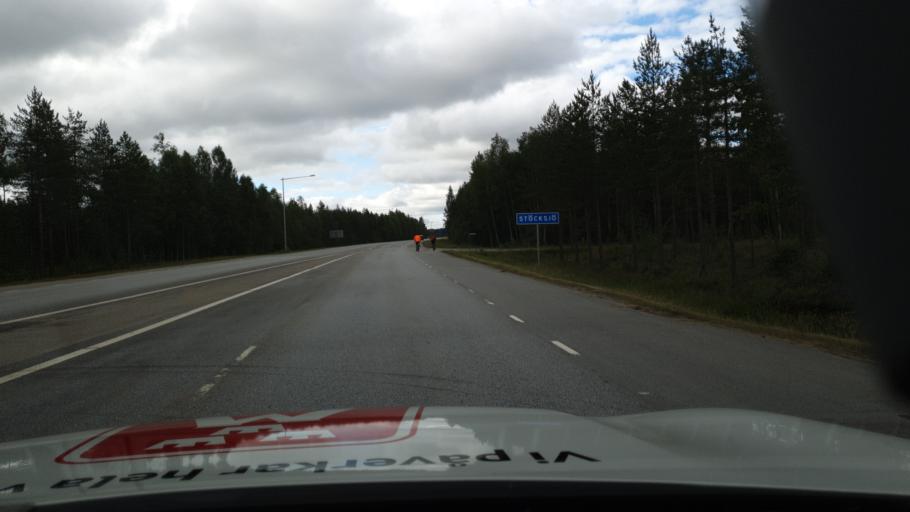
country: SE
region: Vaesterbotten
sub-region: Umea Kommun
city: Roback
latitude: 63.7835
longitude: 20.2033
